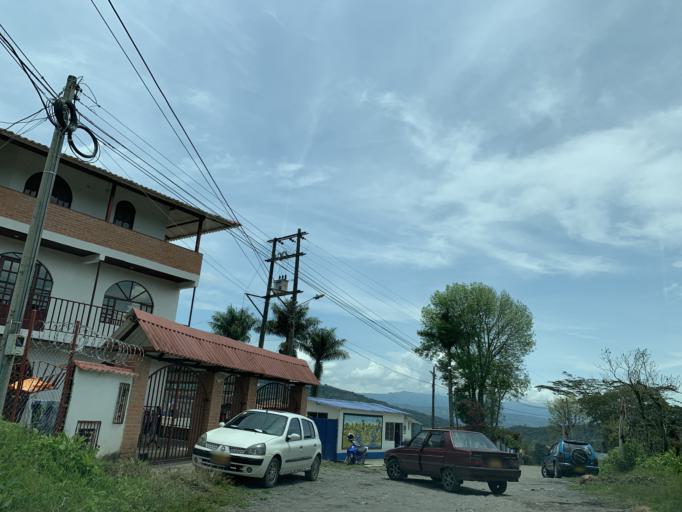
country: CO
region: Boyaca
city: Moniquira
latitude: 5.8734
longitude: -73.5652
